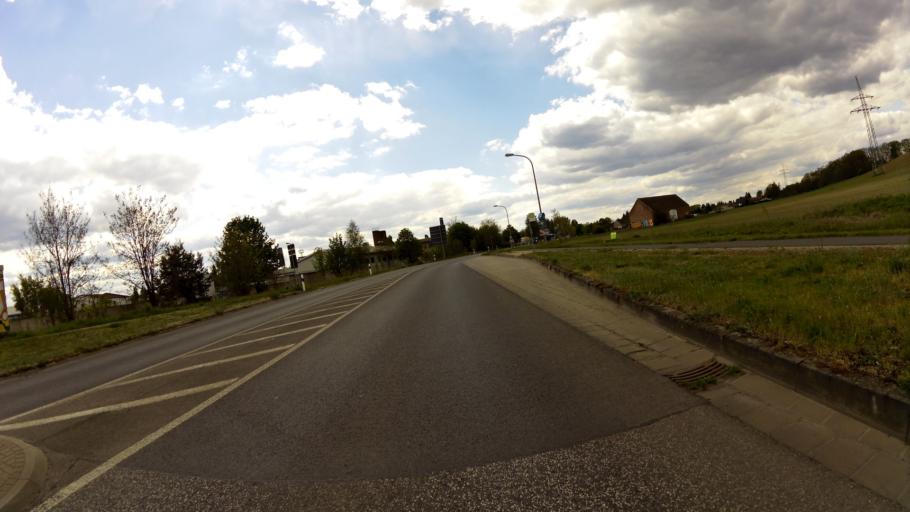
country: DE
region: Brandenburg
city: Furstenwalde
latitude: 52.3799
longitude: 14.0789
